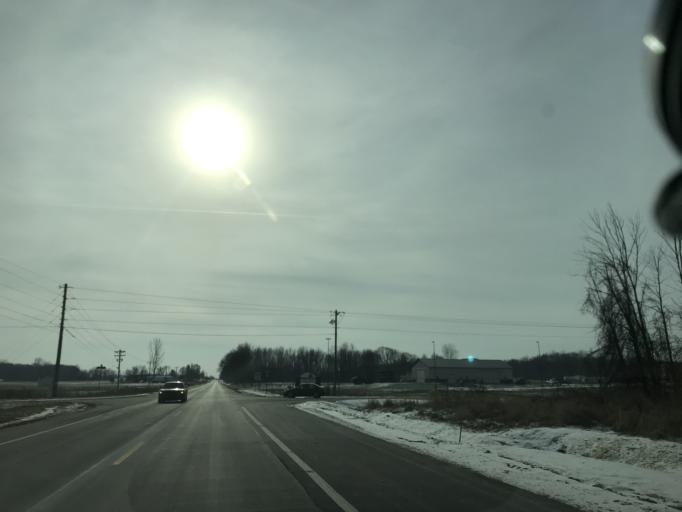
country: US
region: Michigan
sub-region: Ionia County
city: Lake Odessa
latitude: 42.8005
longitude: -85.0745
